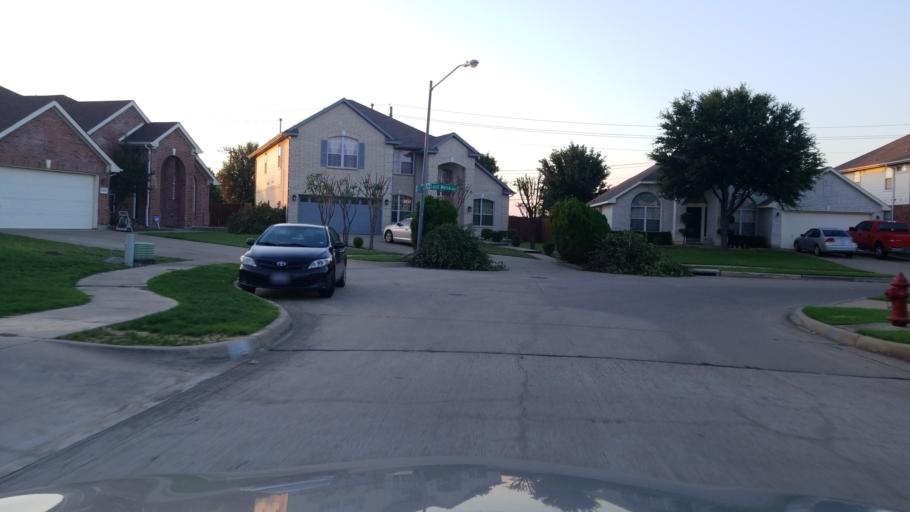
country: US
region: Texas
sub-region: Dallas County
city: Grand Prairie
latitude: 32.6906
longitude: -97.0416
